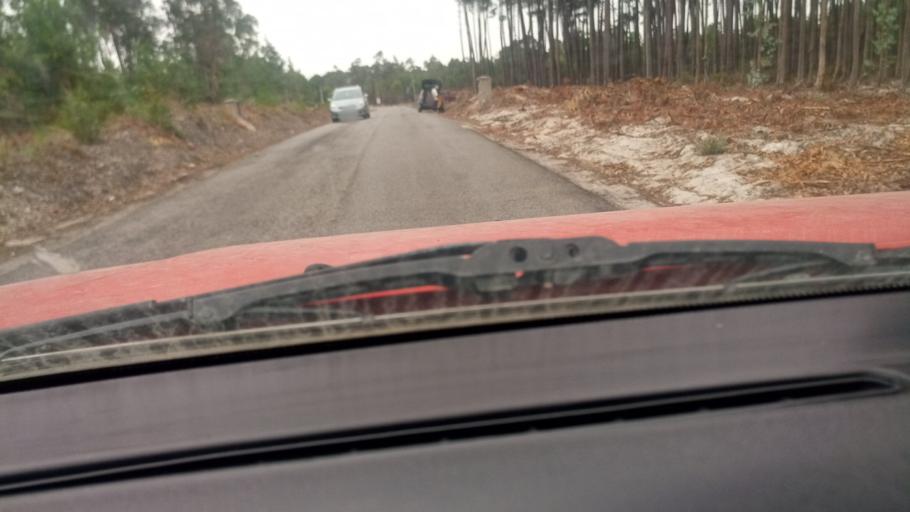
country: PT
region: Leiria
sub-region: Caldas da Rainha
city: Caldas da Rainha
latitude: 39.4448
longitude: -9.1663
